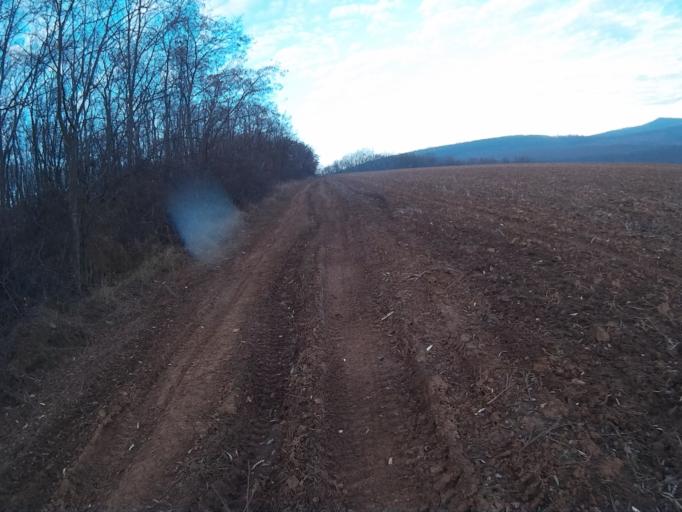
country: HU
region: Nograd
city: Rimoc
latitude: 47.9935
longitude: 19.4301
